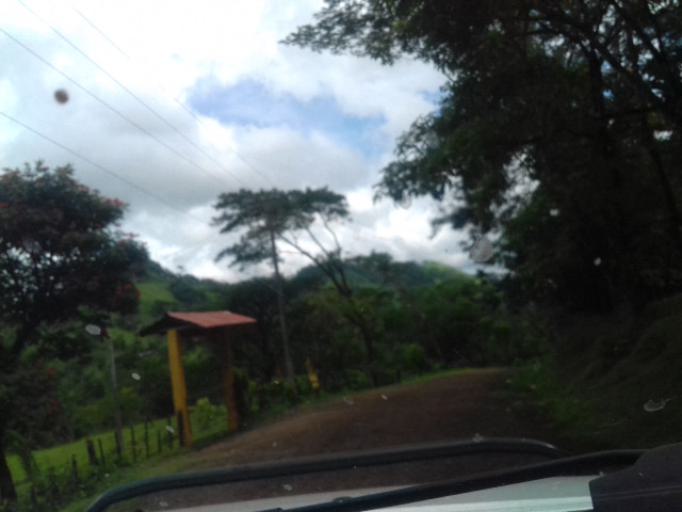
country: NI
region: Matagalpa
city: Rio Blanco
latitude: 13.0314
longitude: -85.2274
